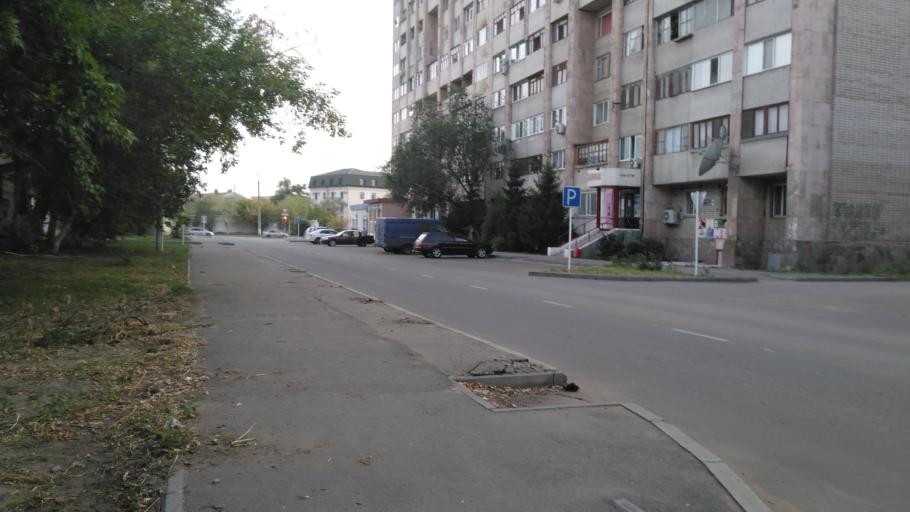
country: KZ
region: Pavlodar
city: Pavlodar
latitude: 52.3000
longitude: 76.9470
